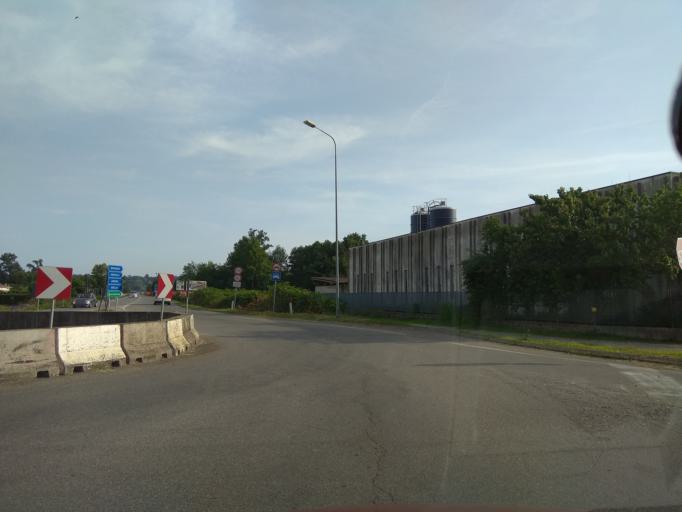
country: IT
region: Piedmont
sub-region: Provincia di Biella
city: Cerreto Castello
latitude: 45.5589
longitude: 8.1679
